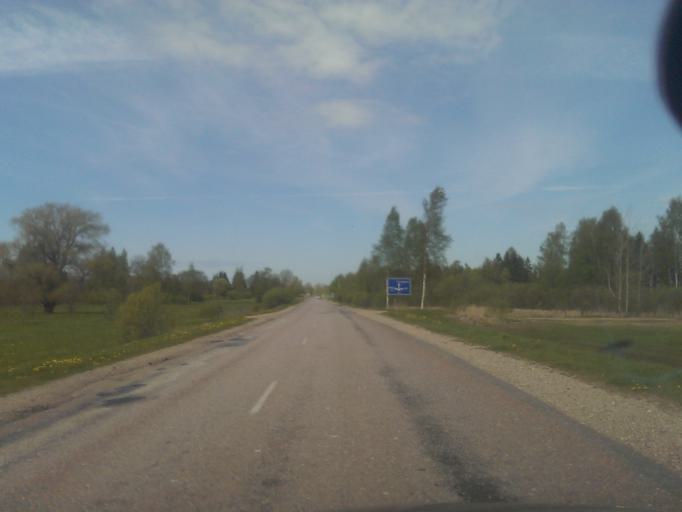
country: LV
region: Ventspils Rajons
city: Piltene
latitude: 57.2716
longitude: 21.5826
